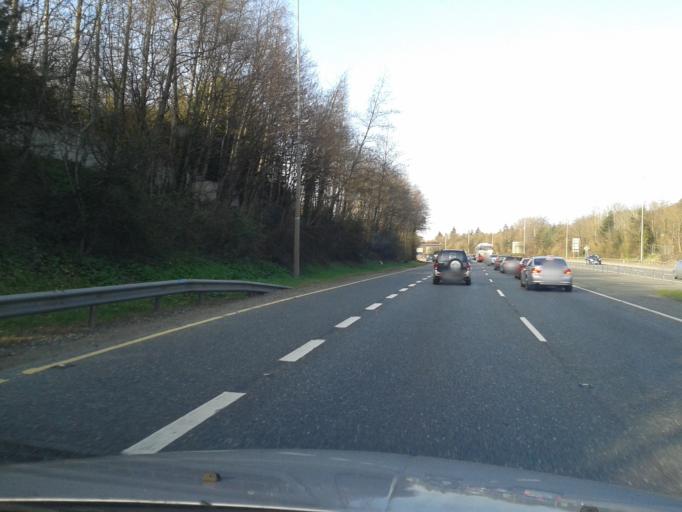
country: IE
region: Leinster
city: Little Bray
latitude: 53.1929
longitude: -6.1368
